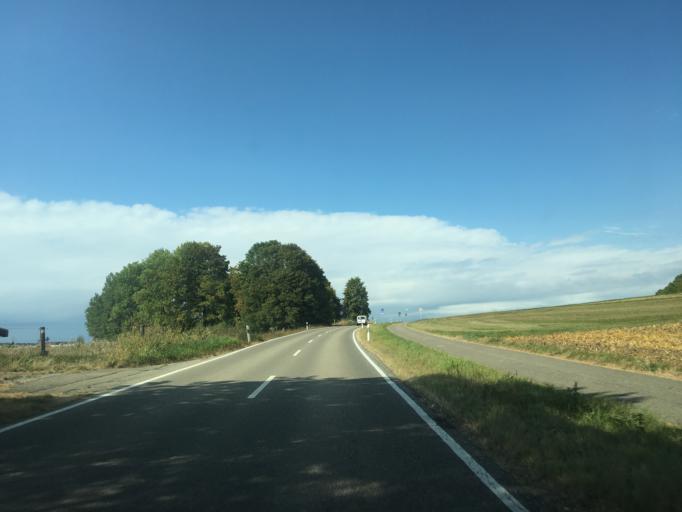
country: DE
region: Baden-Wuerttemberg
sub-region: Tuebingen Region
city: Trochtelfingen
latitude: 48.3808
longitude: 9.1942
